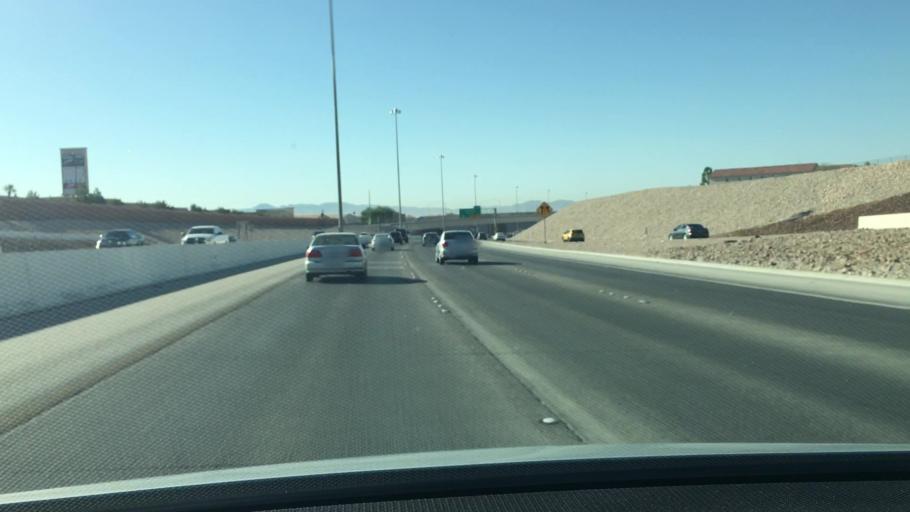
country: US
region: Nevada
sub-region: Clark County
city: Summerlin South
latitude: 36.1134
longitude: -115.3005
